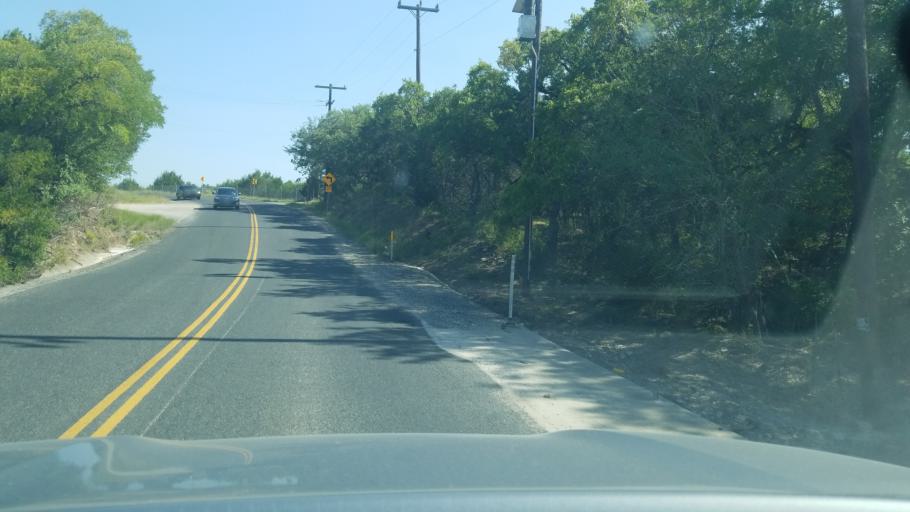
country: US
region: Texas
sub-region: Bexar County
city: Timberwood Park
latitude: 29.7428
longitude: -98.5145
